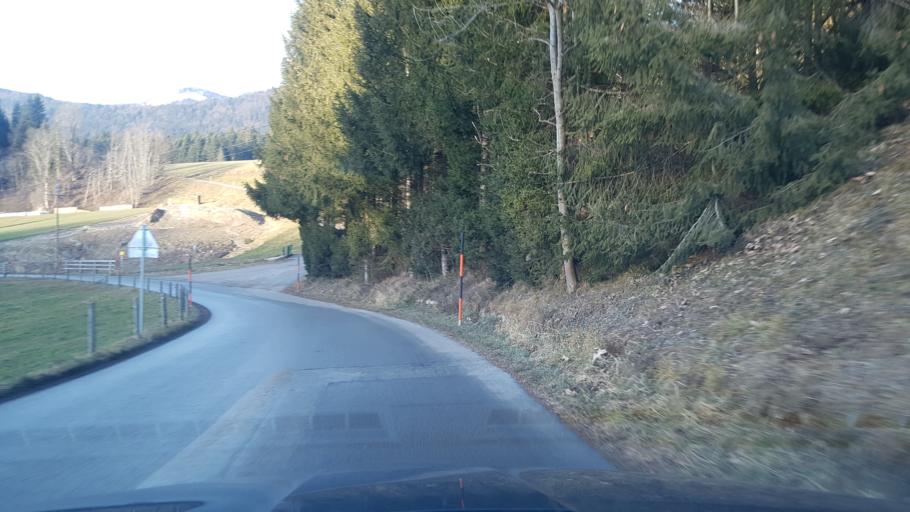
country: AT
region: Salzburg
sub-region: Politischer Bezirk Hallein
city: Abtenau
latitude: 47.5883
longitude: 13.3431
